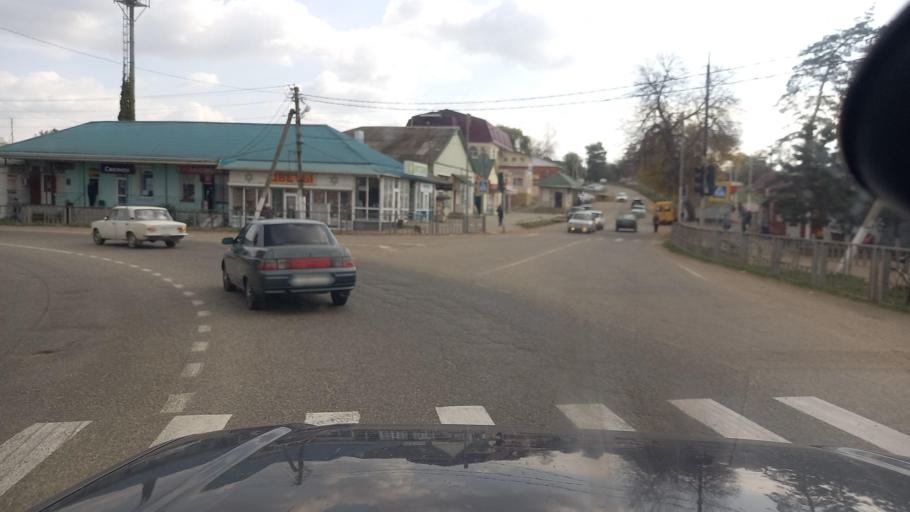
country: RU
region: Krasnodarskiy
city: Kholmskiy
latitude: 44.8434
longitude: 38.3931
